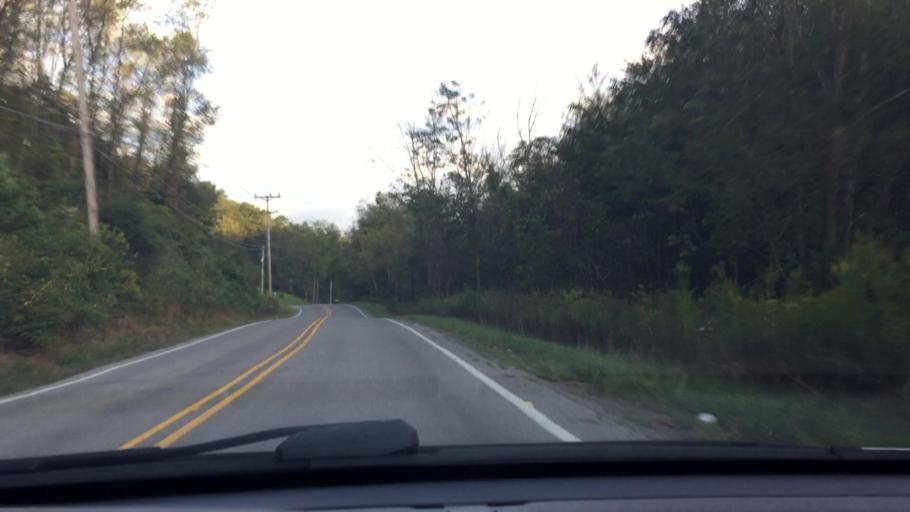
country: US
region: Pennsylvania
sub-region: Westmoreland County
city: Murrysville
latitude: 40.4508
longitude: -79.7262
